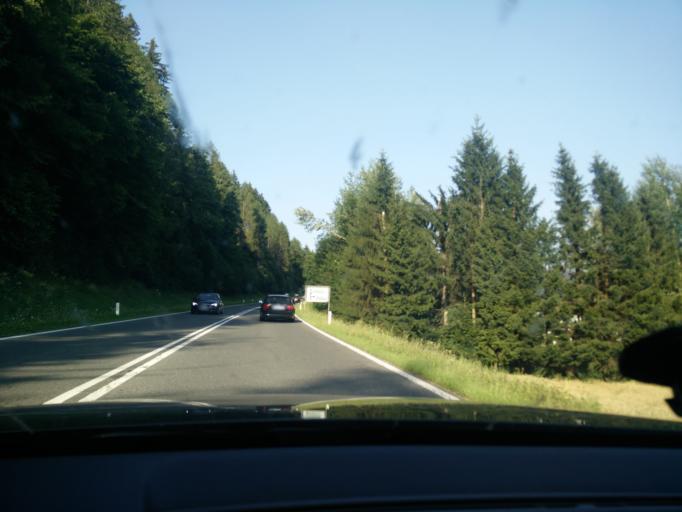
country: AT
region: Carinthia
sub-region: Villach Stadt
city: Villach
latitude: 46.6572
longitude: 13.8850
